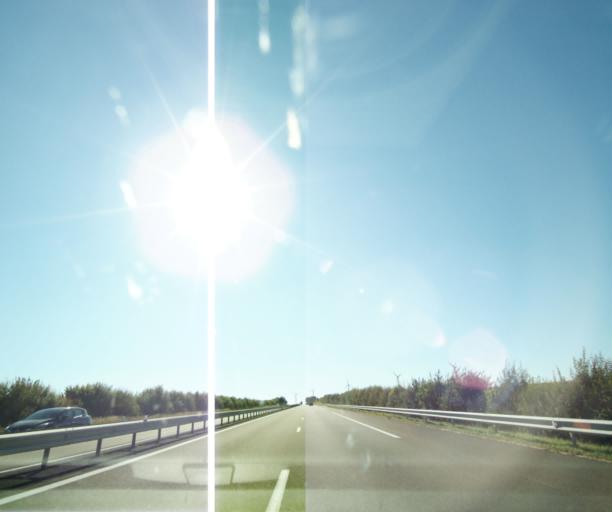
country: FR
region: Champagne-Ardenne
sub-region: Departement de l'Aube
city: Vendeuvre-sur-Barse
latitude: 48.1680
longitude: 4.4880
